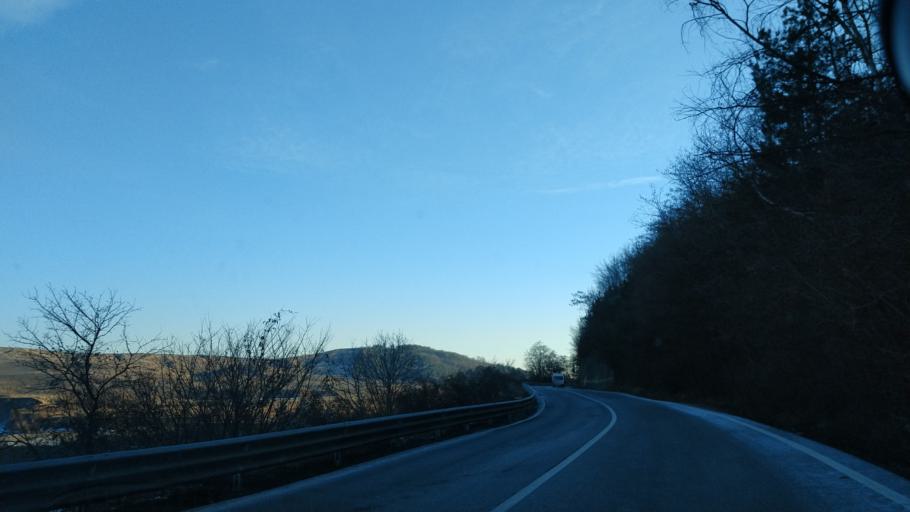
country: RO
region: Bacau
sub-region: Comuna Helegiu
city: Bratila
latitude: 46.3069
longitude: 26.7509
